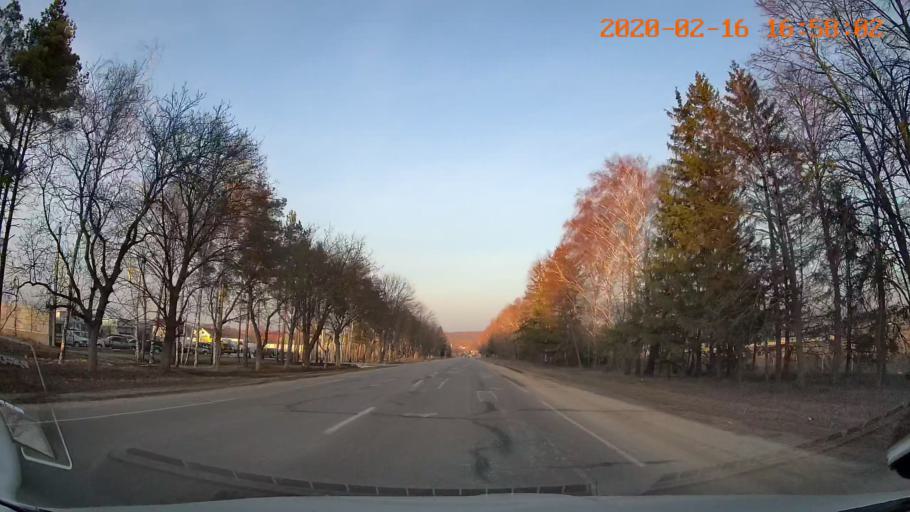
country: MD
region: Briceni
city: Briceni
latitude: 48.3479
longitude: 27.0775
